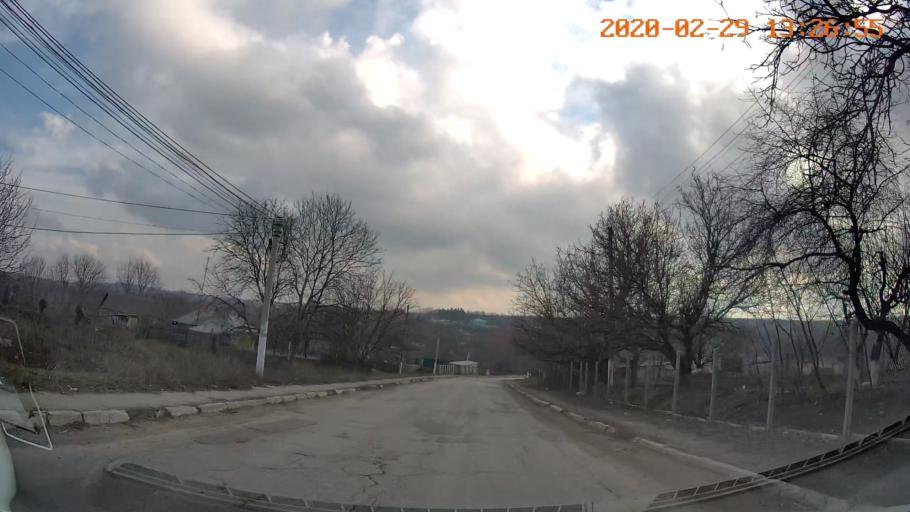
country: MD
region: Telenesti
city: Camenca
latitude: 47.9161
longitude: 28.6397
